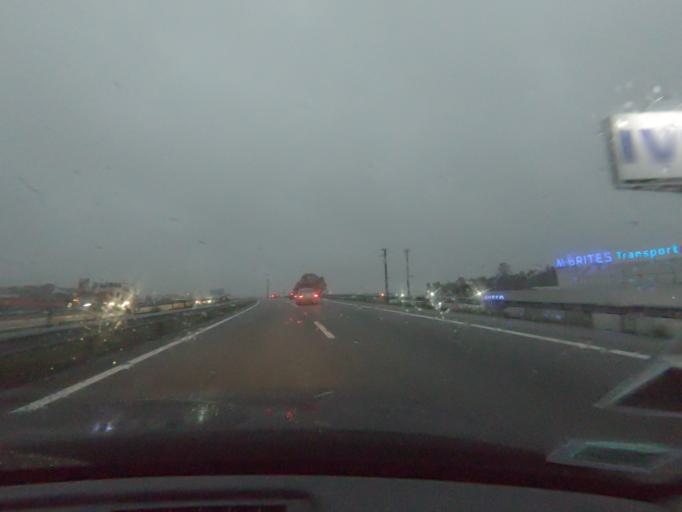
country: PT
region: Porto
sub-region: Matosinhos
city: Santa Cruz do Bispo
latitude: 41.2392
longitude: -8.6957
